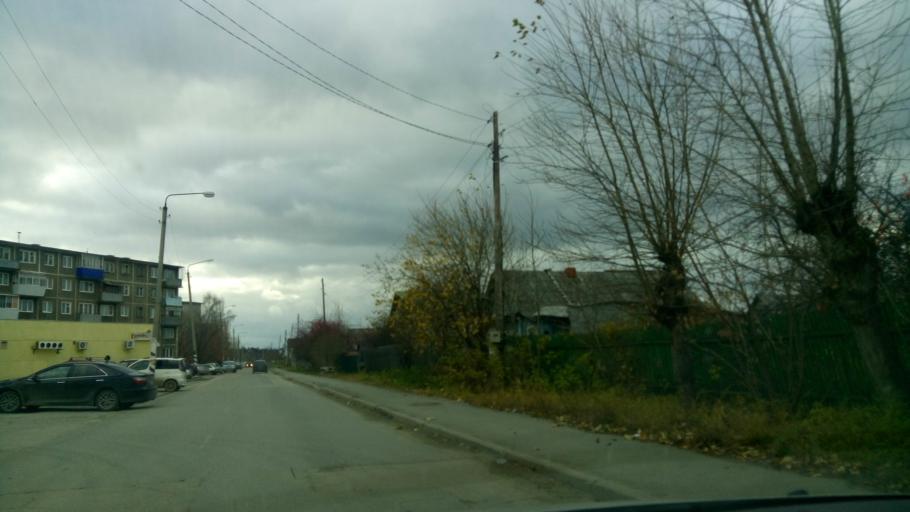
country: RU
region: Sverdlovsk
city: Sredneuralsk
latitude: 56.9835
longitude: 60.4717
